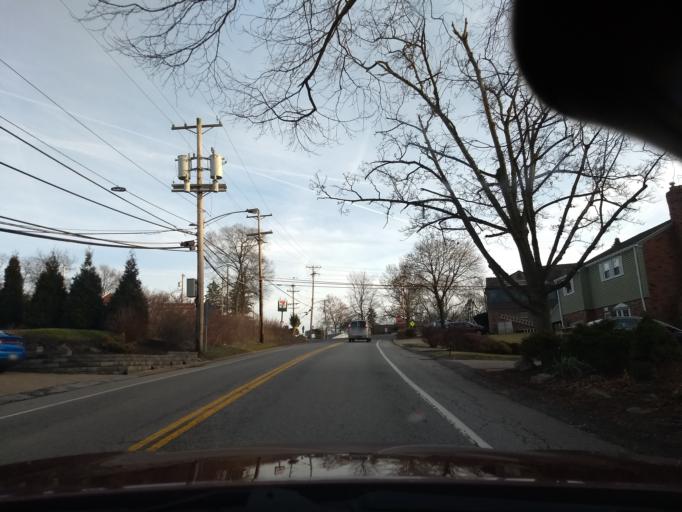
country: US
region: Pennsylvania
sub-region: Allegheny County
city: Brentwood
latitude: 40.3642
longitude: -79.9688
